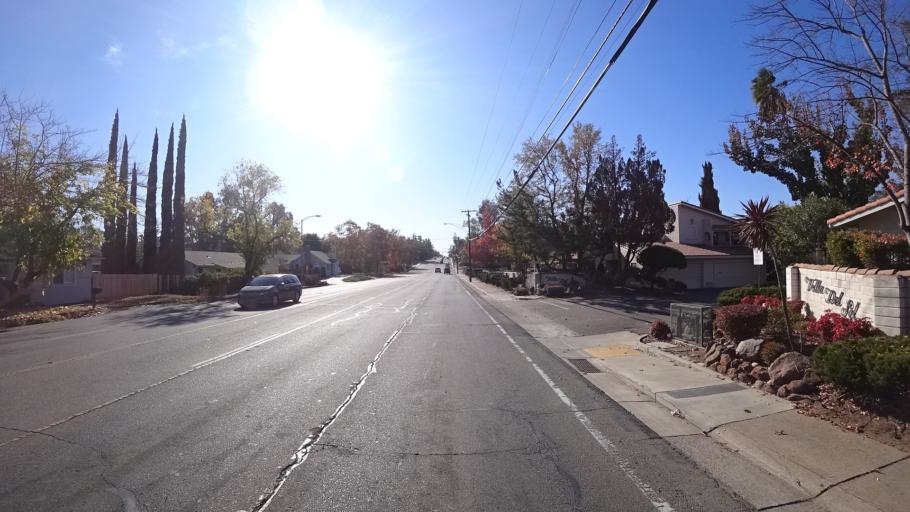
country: US
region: California
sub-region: Sacramento County
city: Fair Oaks
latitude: 38.6714
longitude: -121.2923
